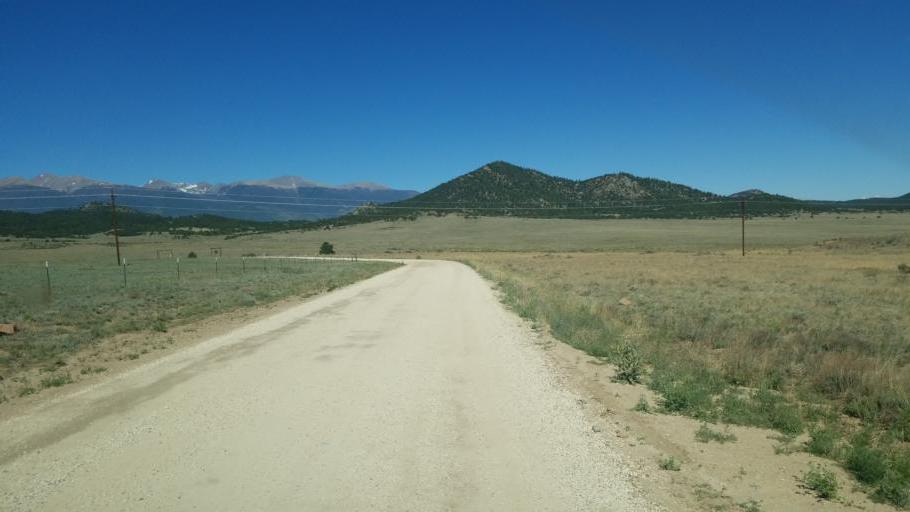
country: US
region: Colorado
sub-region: Custer County
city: Westcliffe
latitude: 38.2342
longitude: -105.4992
